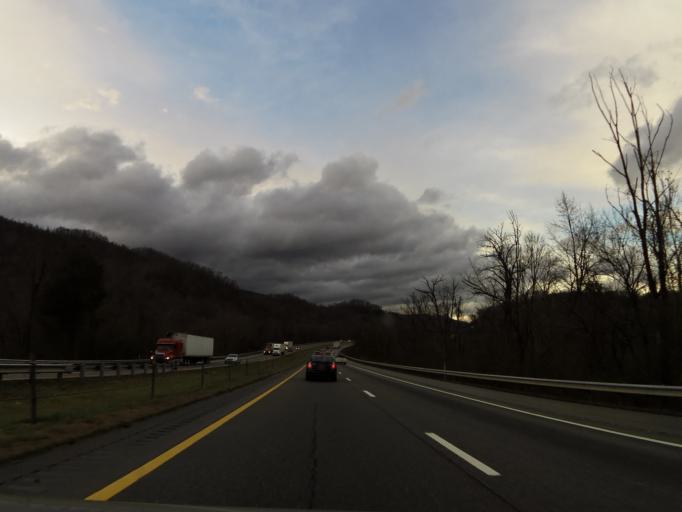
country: US
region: Tennessee
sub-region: Campbell County
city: Caryville
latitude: 36.2727
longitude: -84.1999
